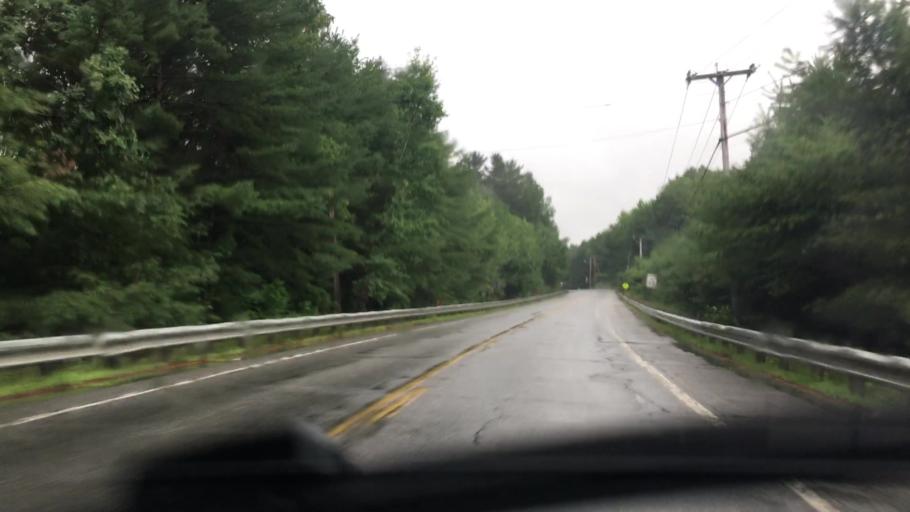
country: US
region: Maine
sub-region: Kennebec County
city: Pittston
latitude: 44.1969
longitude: -69.7608
